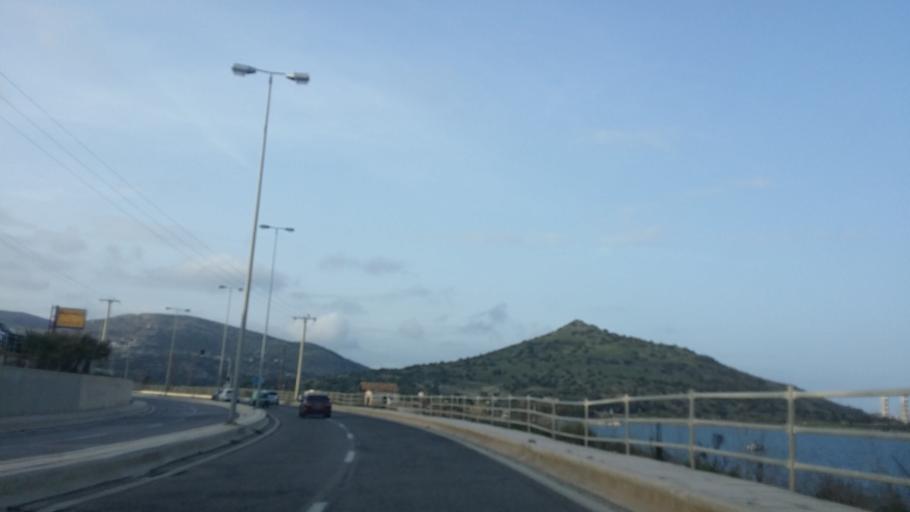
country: GR
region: Attica
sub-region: Nomarchia Anatolikis Attikis
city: Lavrio
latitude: 37.7296
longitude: 24.0534
